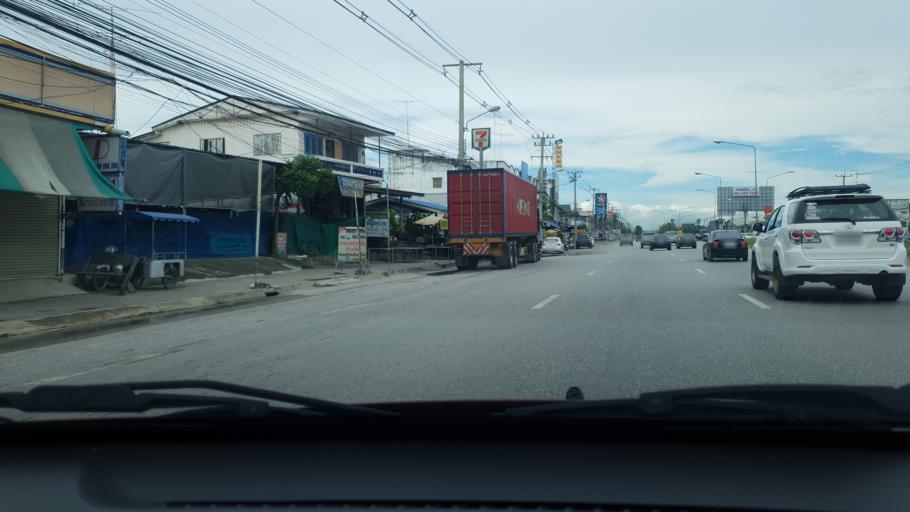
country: TH
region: Phetchaburi
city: Cha-am
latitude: 12.8402
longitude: 99.9304
